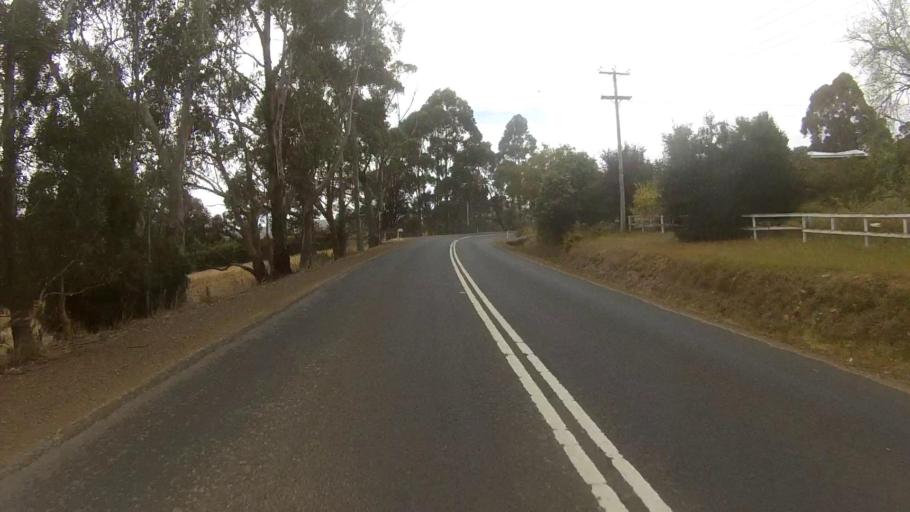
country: AU
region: Tasmania
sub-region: Kingborough
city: Margate
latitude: -43.0141
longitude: 147.2486
